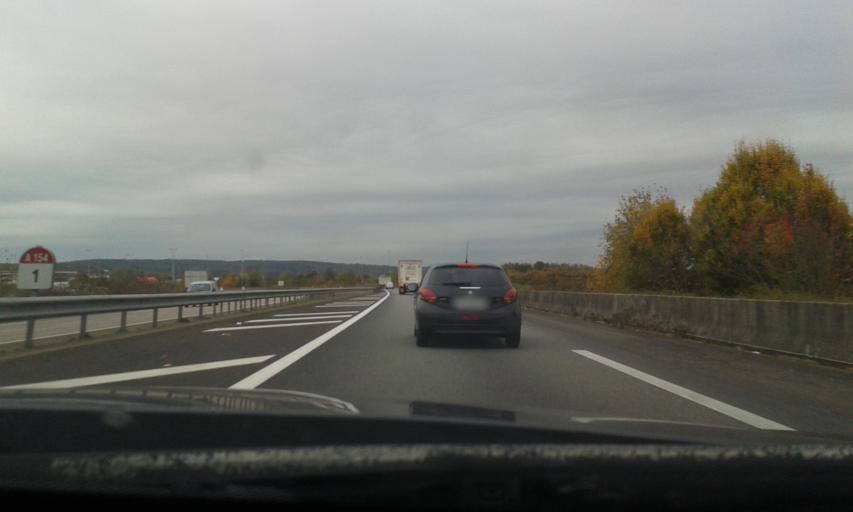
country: FR
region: Haute-Normandie
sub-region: Departement de l'Eure
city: Le Vaudreuil
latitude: 49.2424
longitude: 1.1864
